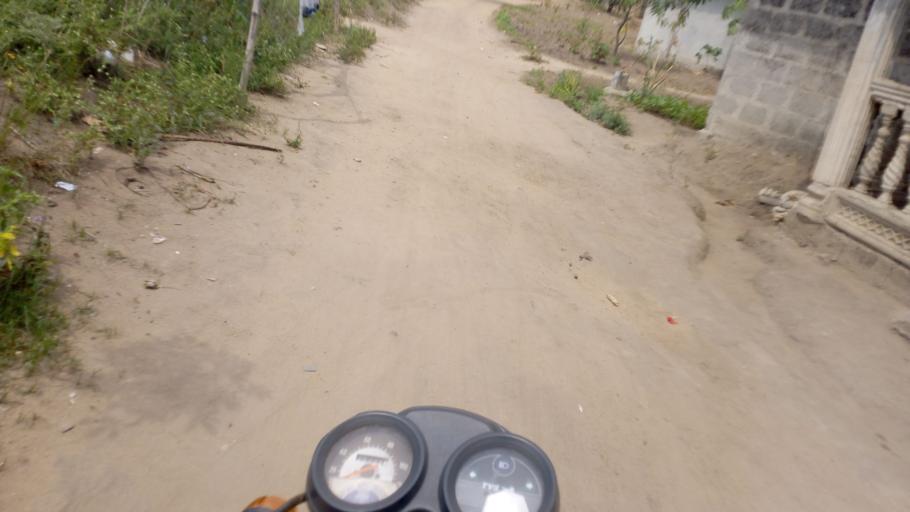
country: SL
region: Western Area
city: Waterloo
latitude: 8.3112
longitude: -13.0631
